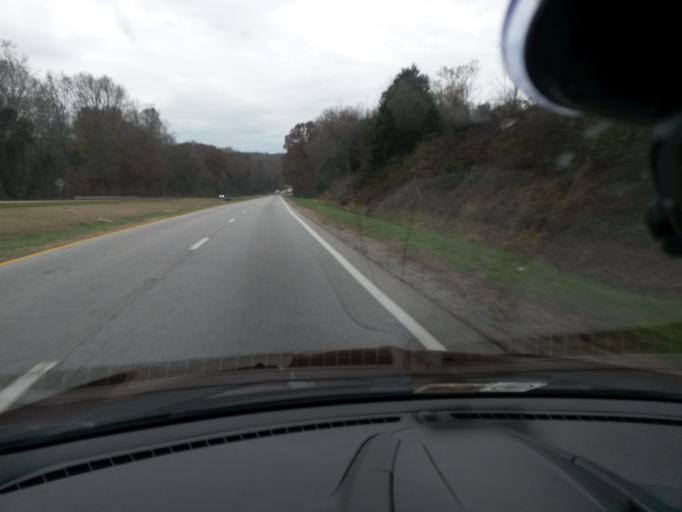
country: US
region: Virginia
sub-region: Amherst County
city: Amherst
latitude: 37.6617
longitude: -78.9558
